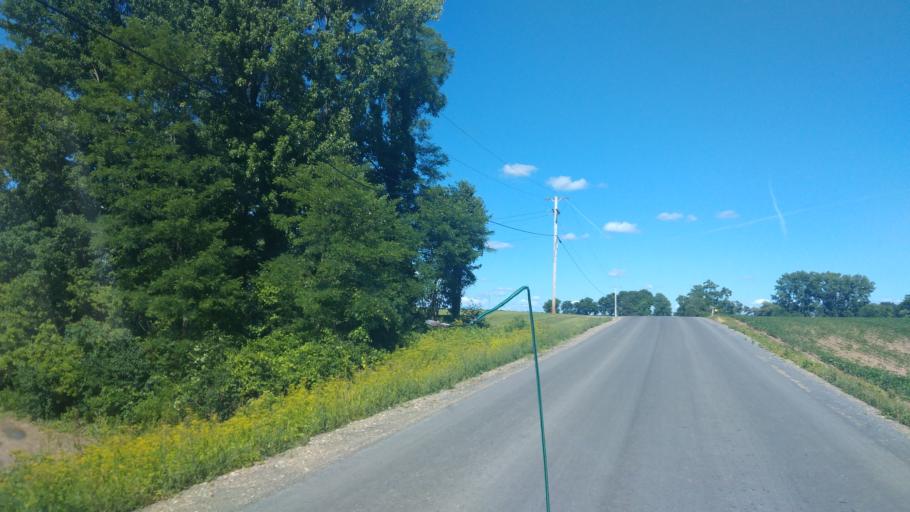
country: US
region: New York
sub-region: Wayne County
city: Clyde
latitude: 43.0256
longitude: -76.9060
